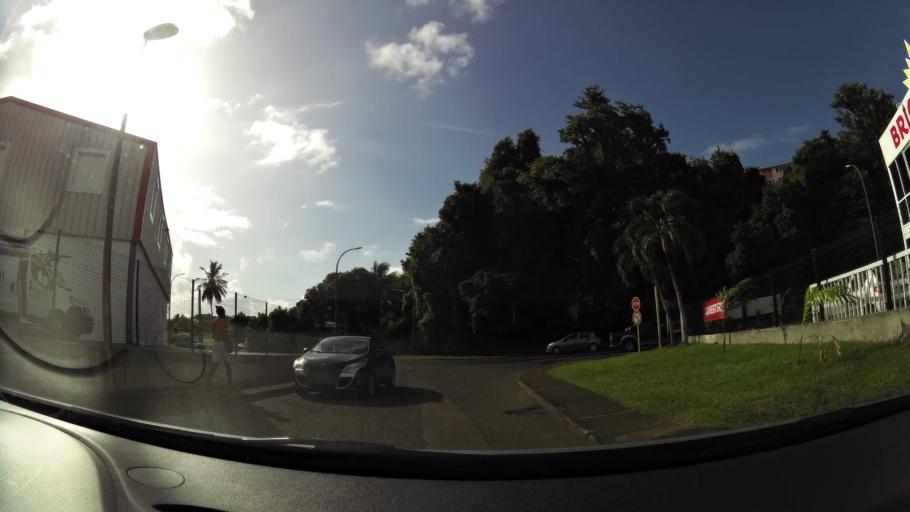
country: MQ
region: Martinique
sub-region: Martinique
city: Saint-Esprit
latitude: 14.5236
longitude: -60.9770
